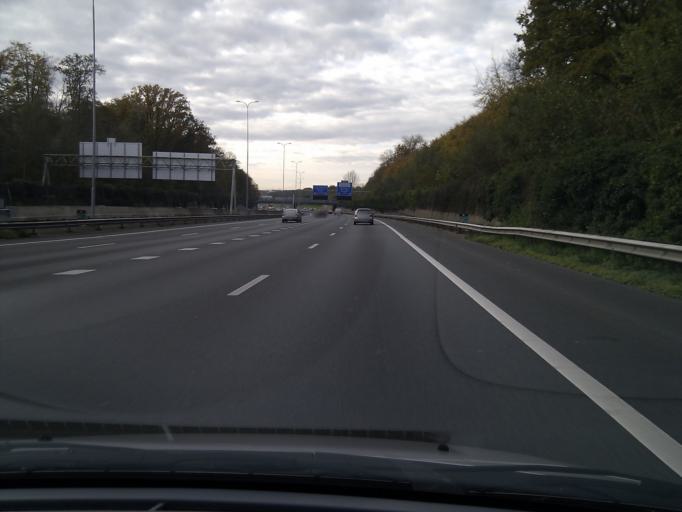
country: NL
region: Utrecht
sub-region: Gemeente Utrecht
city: Lunetten
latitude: 52.0739
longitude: 5.1537
